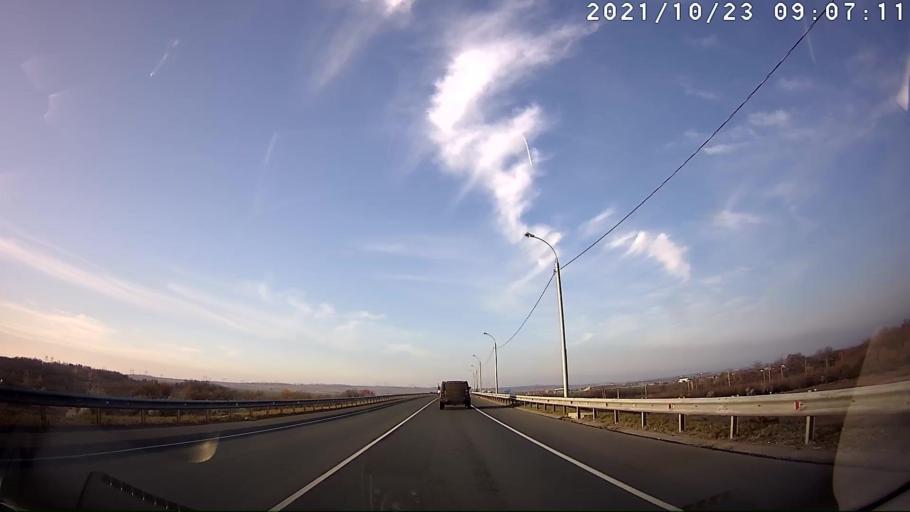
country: RU
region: Saratov
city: Yelshanka
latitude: 51.8022
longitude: 46.1901
